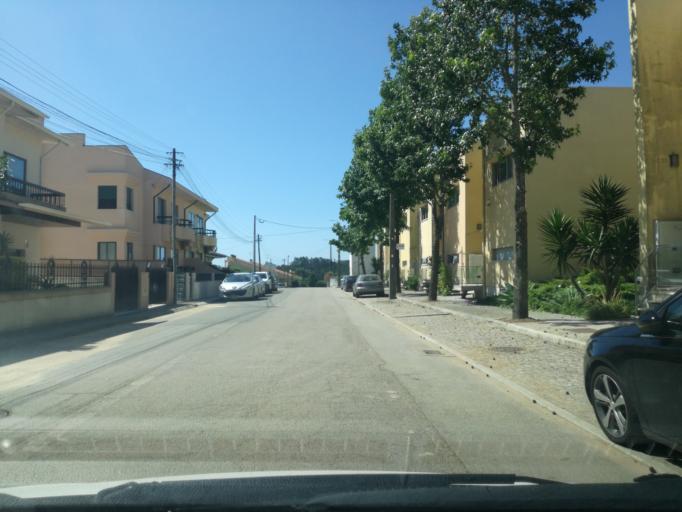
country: PT
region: Porto
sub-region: Maia
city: Gemunde
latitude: 41.2706
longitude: -8.6375
